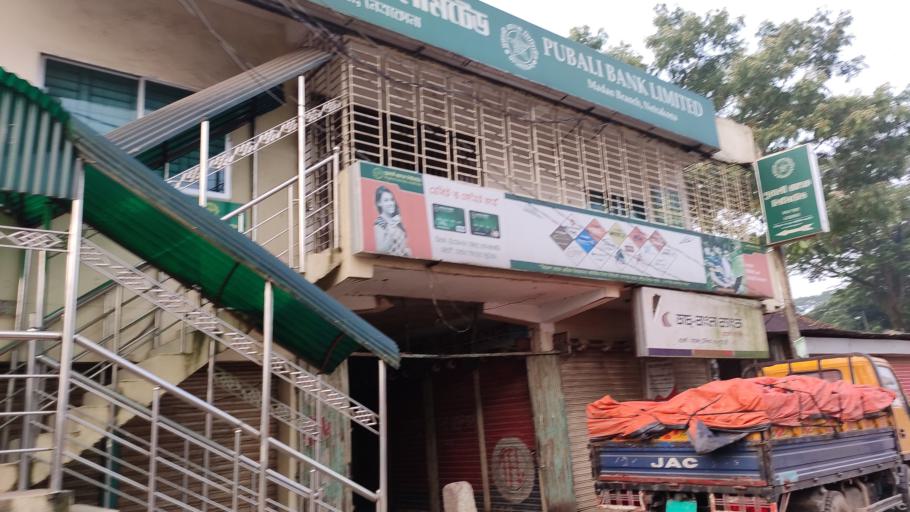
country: BD
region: Dhaka
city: Netrakona
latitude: 24.7167
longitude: 90.9498
